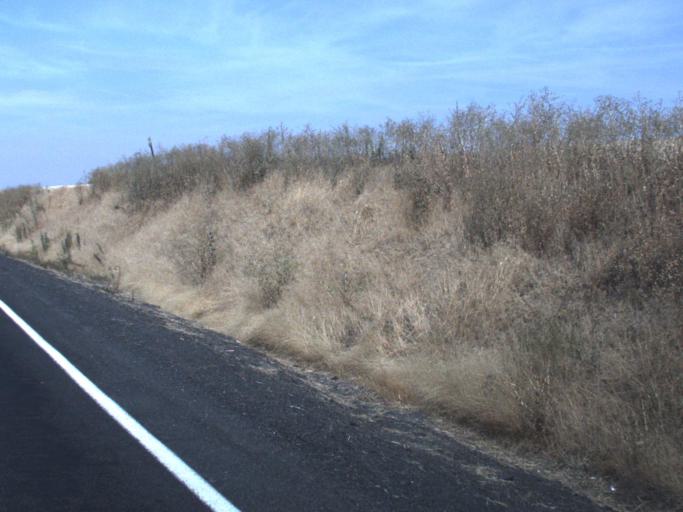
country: US
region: Idaho
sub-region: Latah County
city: Moscow
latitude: 46.9216
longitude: -117.0871
